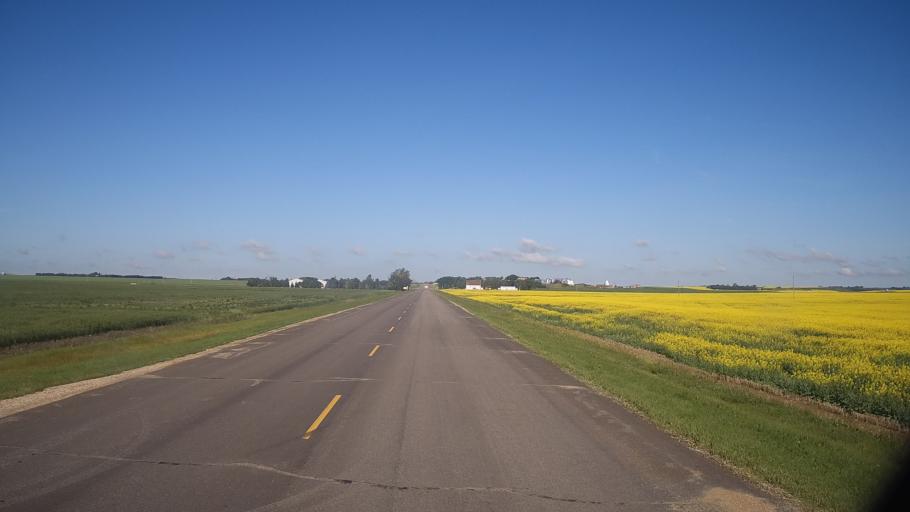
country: CA
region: Saskatchewan
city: Watrous
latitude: 51.6780
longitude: -105.3923
